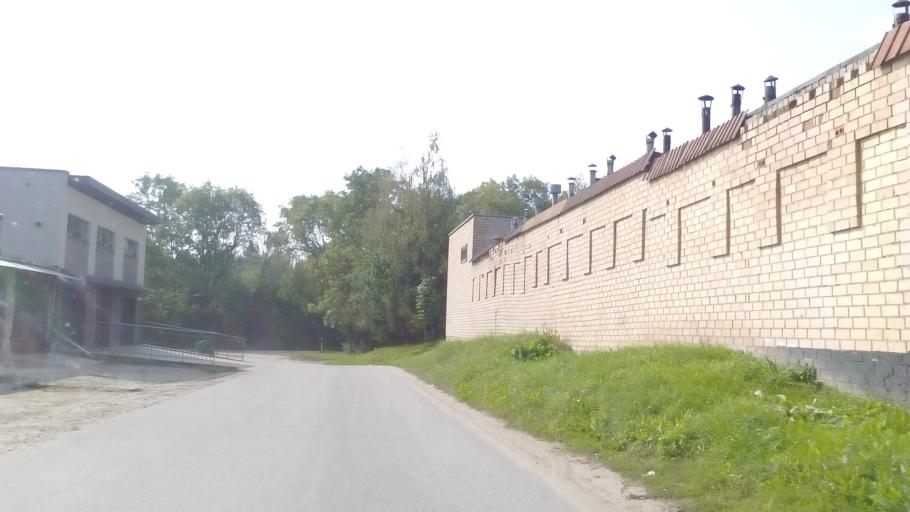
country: LT
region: Alytaus apskritis
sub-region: Alytus
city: Alytus
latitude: 54.3875
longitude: 24.0152
